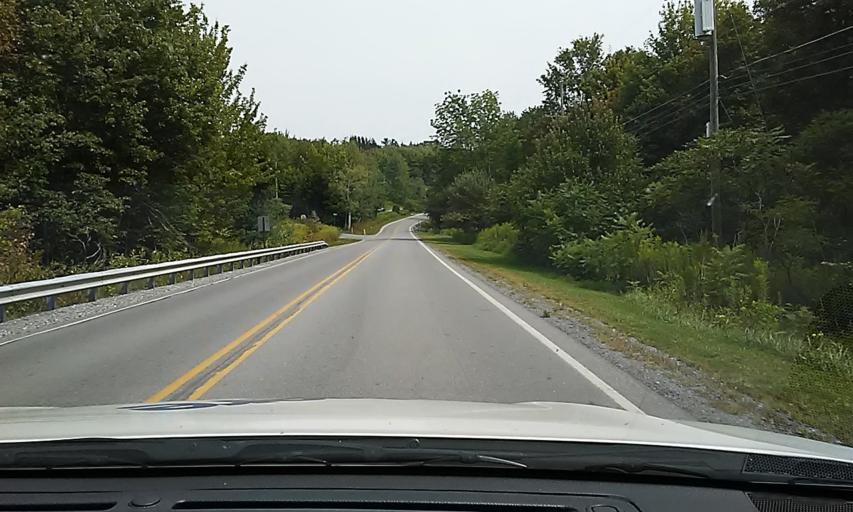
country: US
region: Pennsylvania
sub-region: Elk County
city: Saint Marys
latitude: 41.3425
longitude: -78.6233
